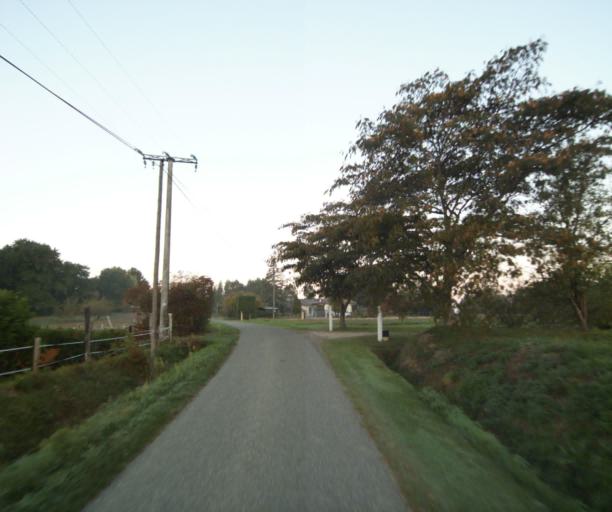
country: FR
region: Midi-Pyrenees
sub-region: Departement du Gers
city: Vic-Fezensac
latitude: 43.7849
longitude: 0.2416
